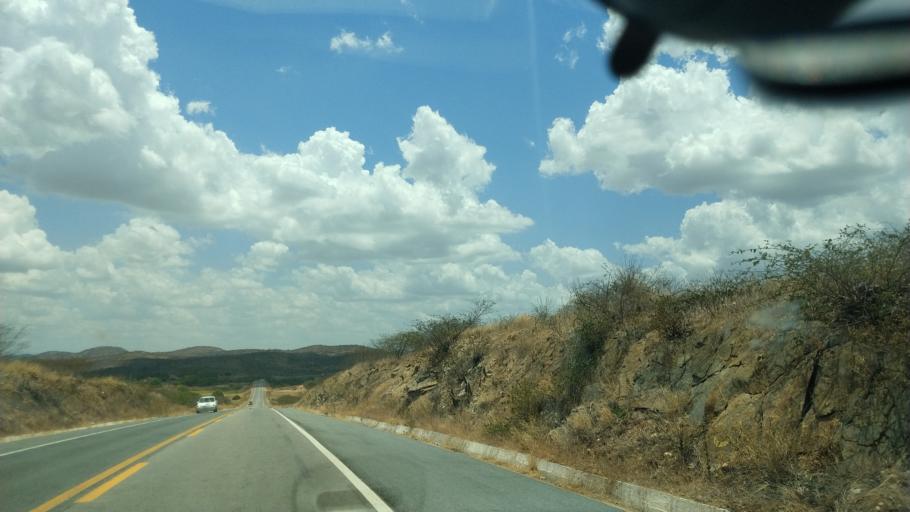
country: BR
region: Rio Grande do Norte
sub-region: Currais Novos
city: Currais Novos
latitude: -6.2496
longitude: -36.4732
